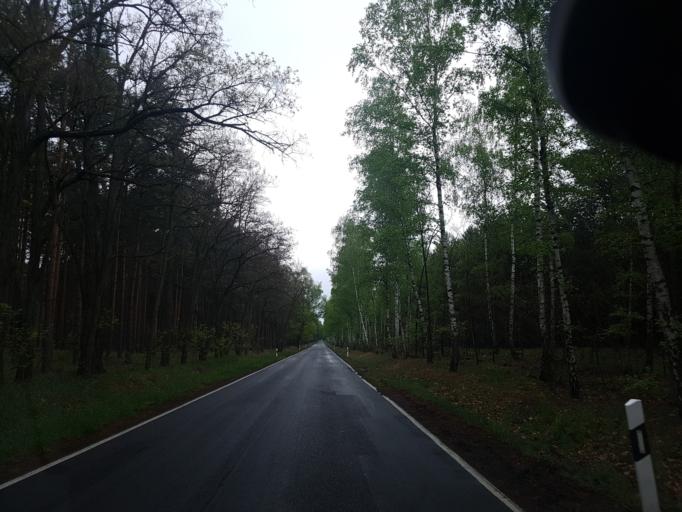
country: DE
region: Brandenburg
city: Spremberg
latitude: 51.6199
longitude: 14.4159
